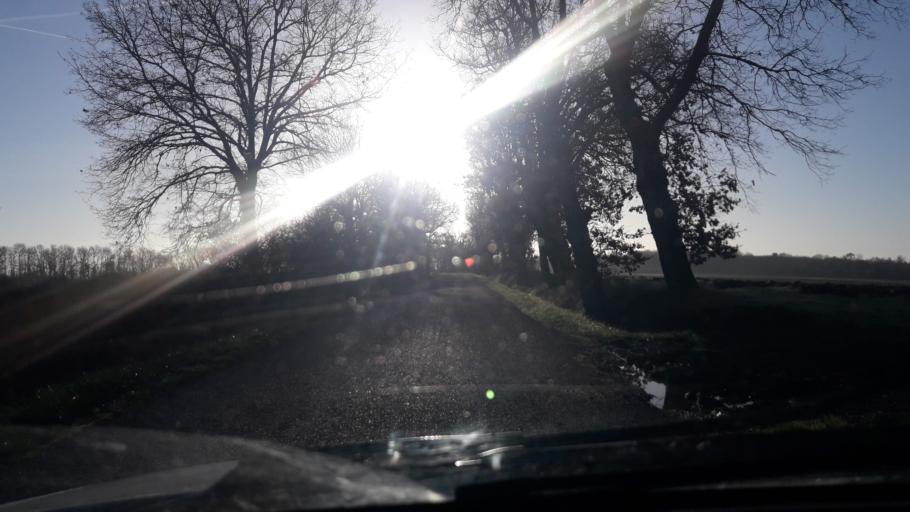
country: FR
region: Midi-Pyrenees
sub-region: Departement du Gers
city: Gimont
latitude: 43.6488
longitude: 0.9917
